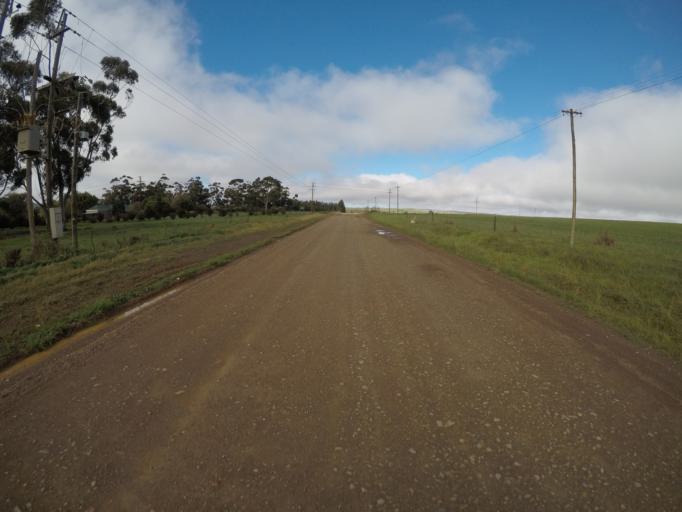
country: ZA
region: Western Cape
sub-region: Cape Winelands District Municipality
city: Ashton
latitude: -34.1389
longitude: 19.8611
